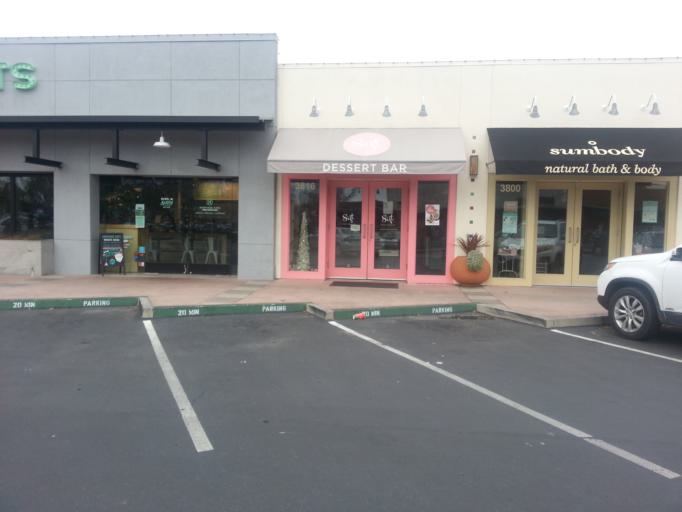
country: US
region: California
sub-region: Napa County
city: Napa
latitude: 38.3238
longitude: -122.3069
